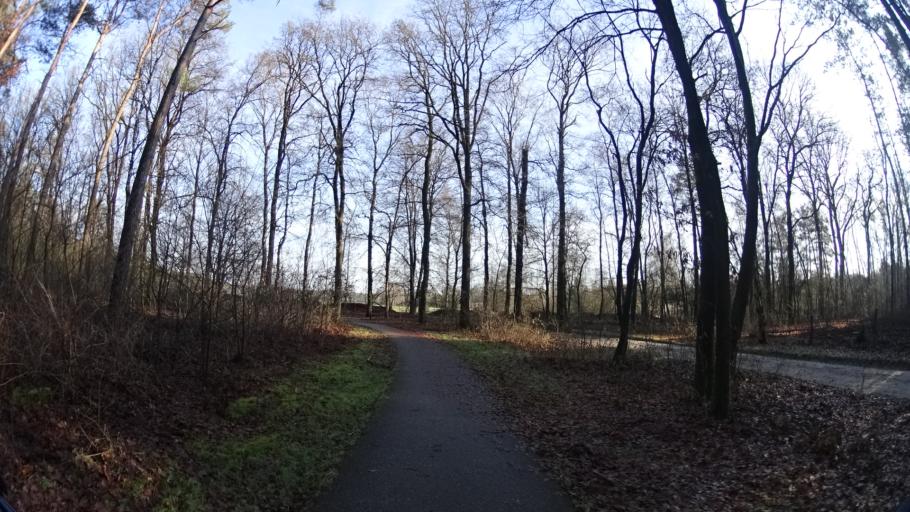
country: NL
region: Gelderland
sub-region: Gemeente Ede
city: Otterlo
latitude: 52.0875
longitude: 5.7641
